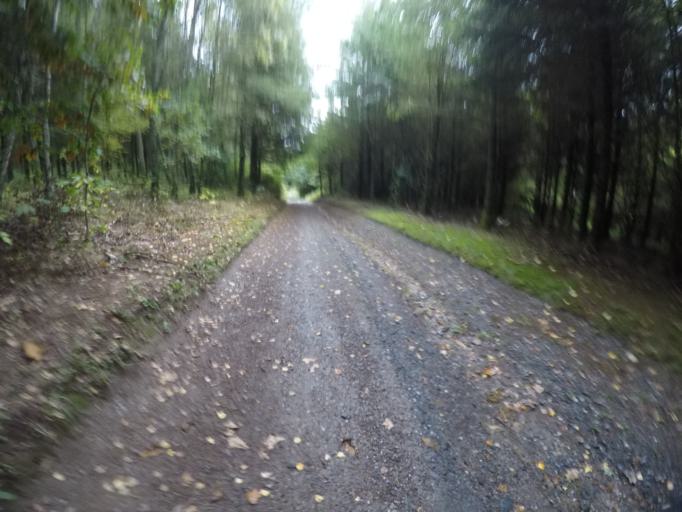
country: BE
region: Wallonia
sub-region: Province du Luxembourg
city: Fauvillers
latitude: 49.8667
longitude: 5.6890
